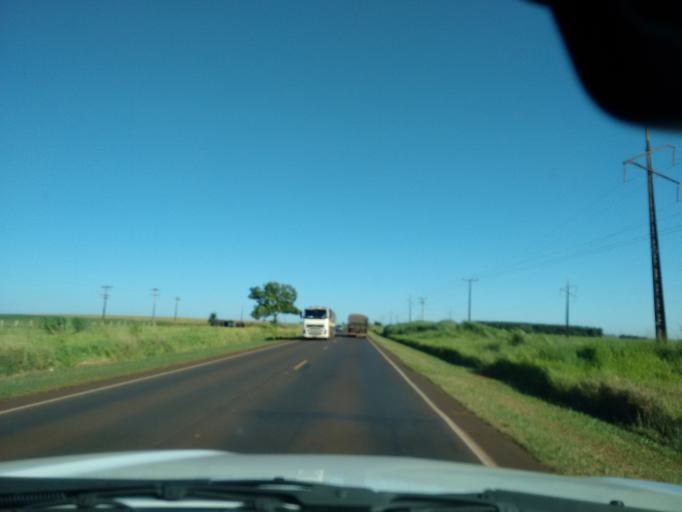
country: BR
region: Mato Grosso do Sul
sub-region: Dourados
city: Dourados
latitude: -22.3724
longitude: -54.7957
